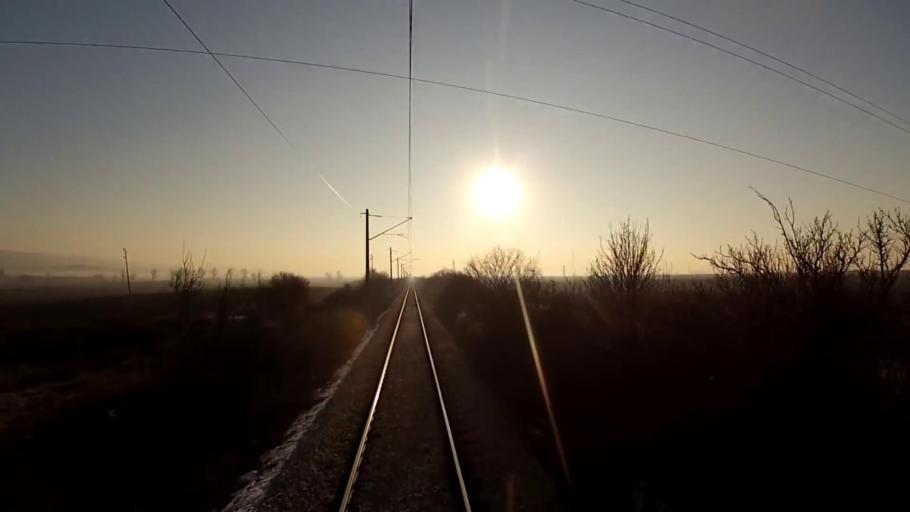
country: BG
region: Sofiya
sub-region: Obshtina Kostinbrod
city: Kostinbrod
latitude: 42.8163
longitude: 23.1819
